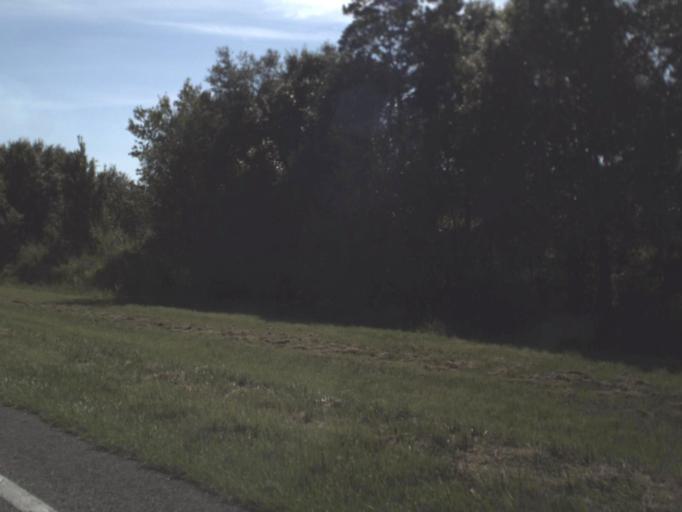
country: US
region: Florida
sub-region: Hendry County
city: Port LaBelle
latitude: 26.9558
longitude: -81.3167
